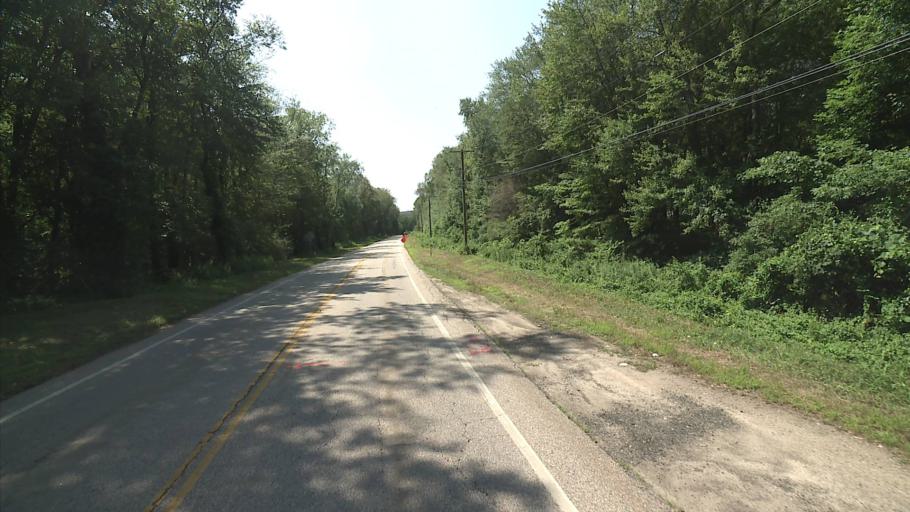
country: US
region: Connecticut
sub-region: New London County
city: Montville Center
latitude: 41.4226
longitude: -72.2140
